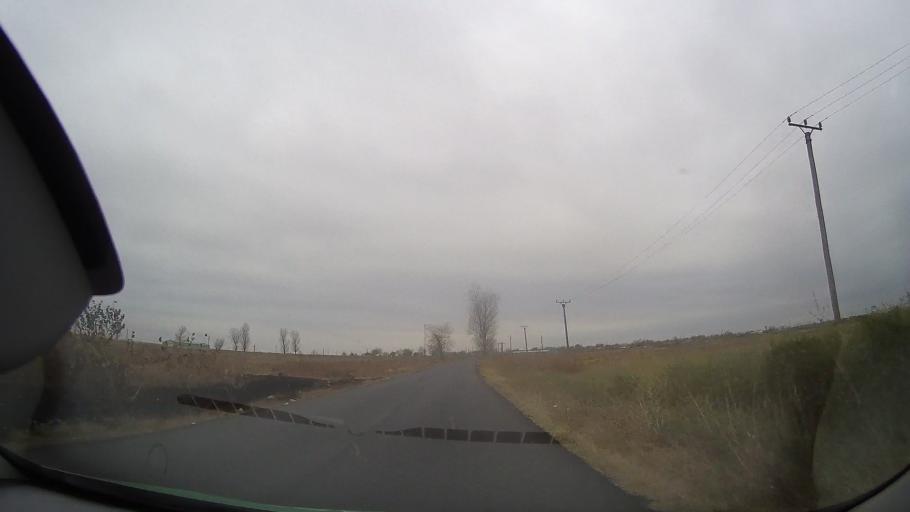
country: RO
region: Braila
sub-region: Comuna Ciresu
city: Ciresu
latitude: 44.9427
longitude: 27.3399
